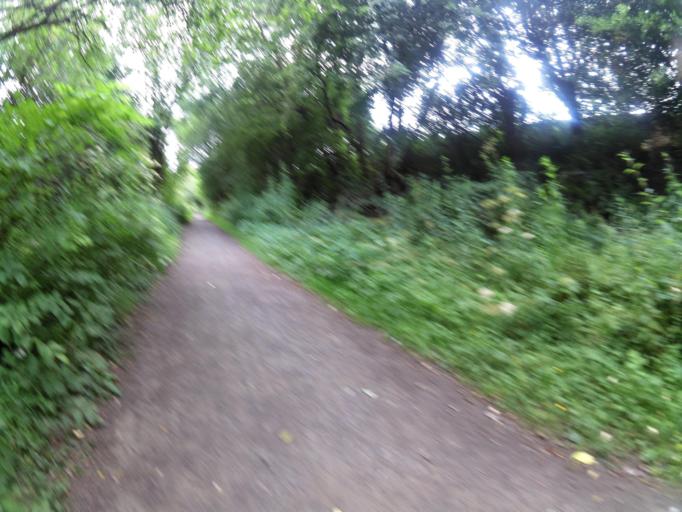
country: GB
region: Scotland
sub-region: Edinburgh
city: Kirkliston
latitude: 55.9585
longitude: -3.3926
